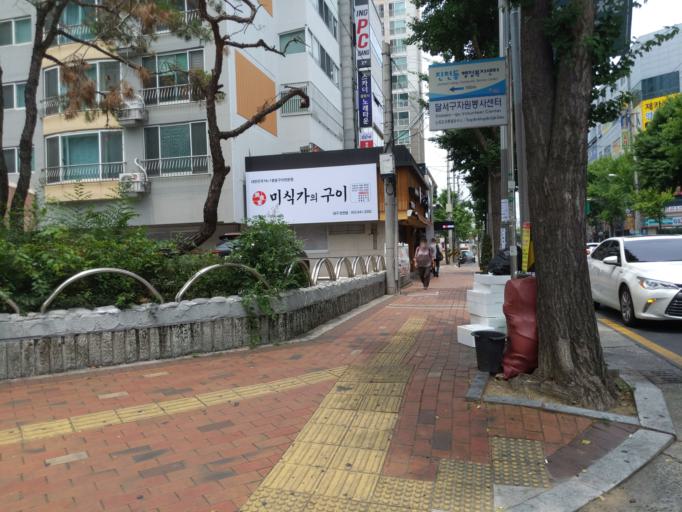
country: KR
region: Daegu
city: Hwawon
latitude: 35.8130
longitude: 128.5246
